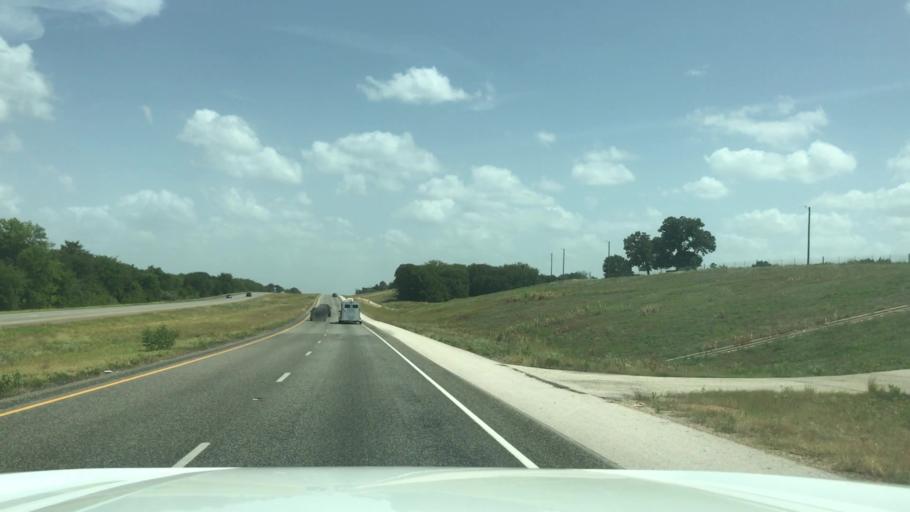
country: US
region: Texas
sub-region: Robertson County
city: Calvert
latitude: 30.9335
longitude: -96.6365
